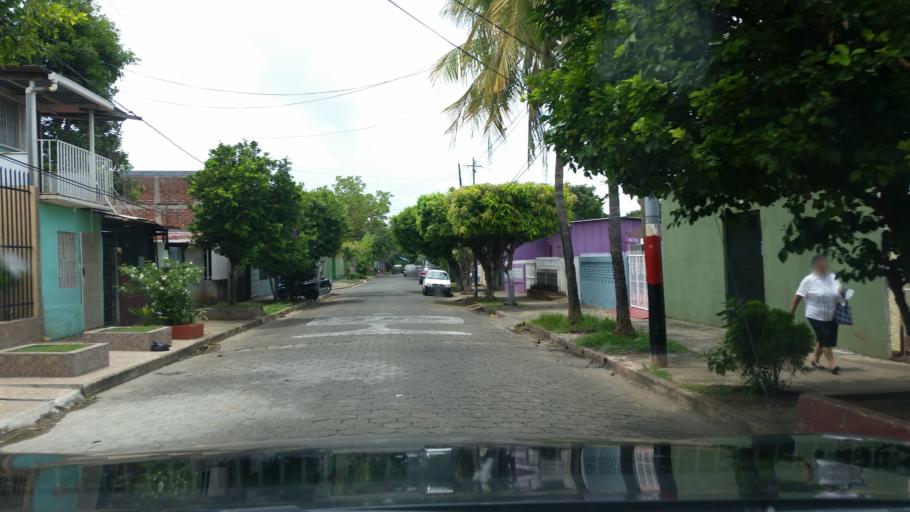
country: NI
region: Managua
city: Managua
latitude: 12.1293
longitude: -86.2601
